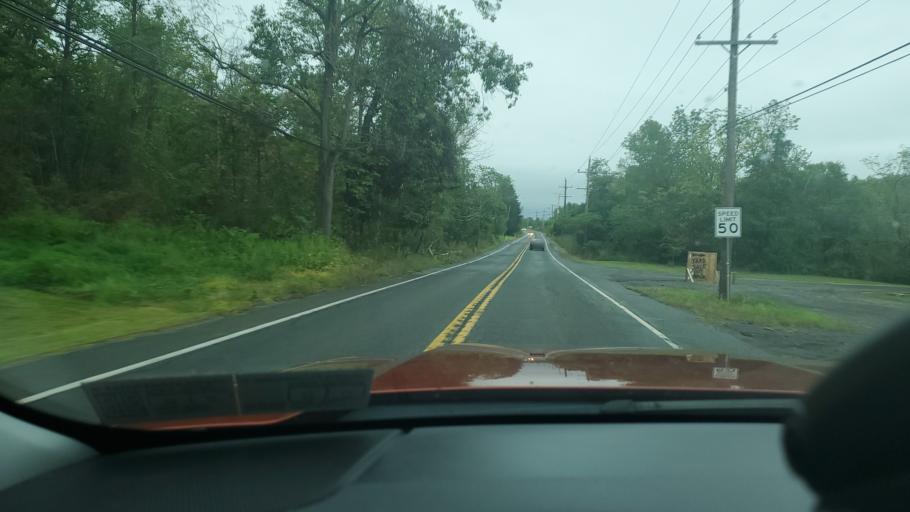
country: US
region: Pennsylvania
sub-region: Montgomery County
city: Woxall
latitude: 40.3106
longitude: -75.4807
